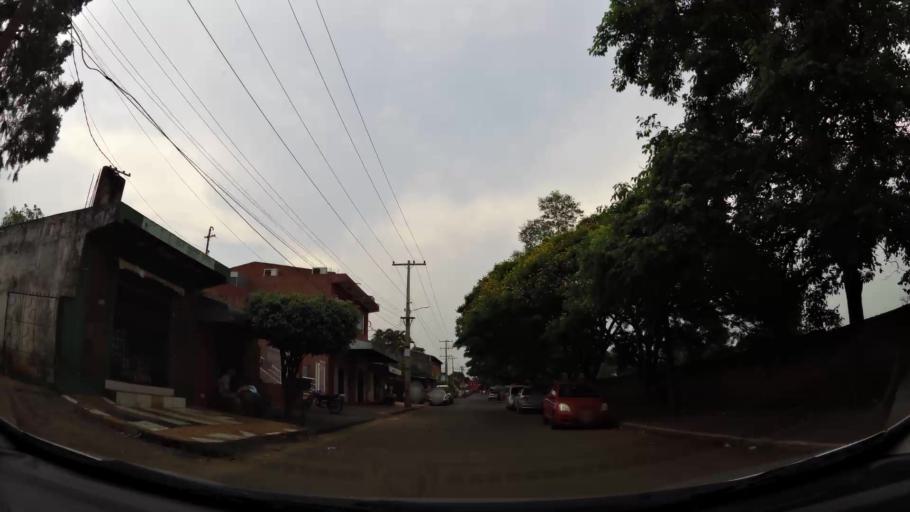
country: PY
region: Alto Parana
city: Presidente Franco
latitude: -25.5359
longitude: -54.6133
